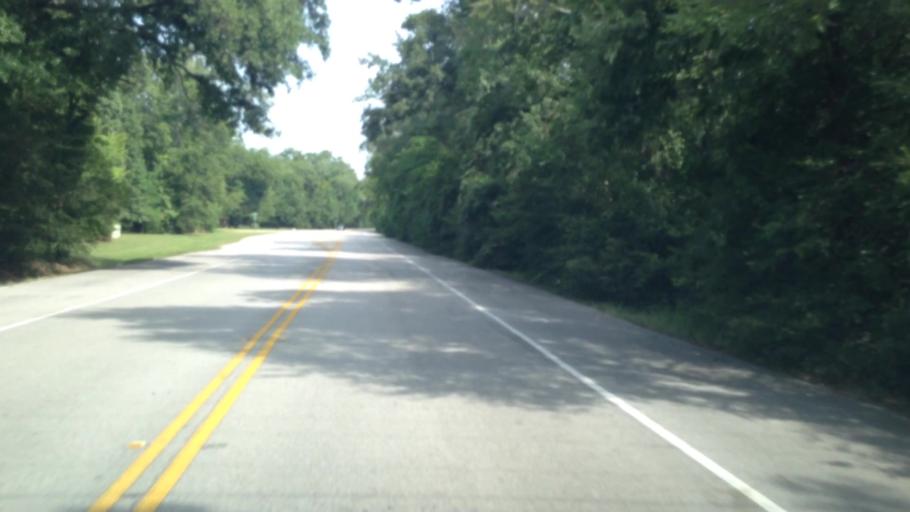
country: US
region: Texas
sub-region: Harris County
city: Sheldon
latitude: 29.9255
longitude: -95.1710
